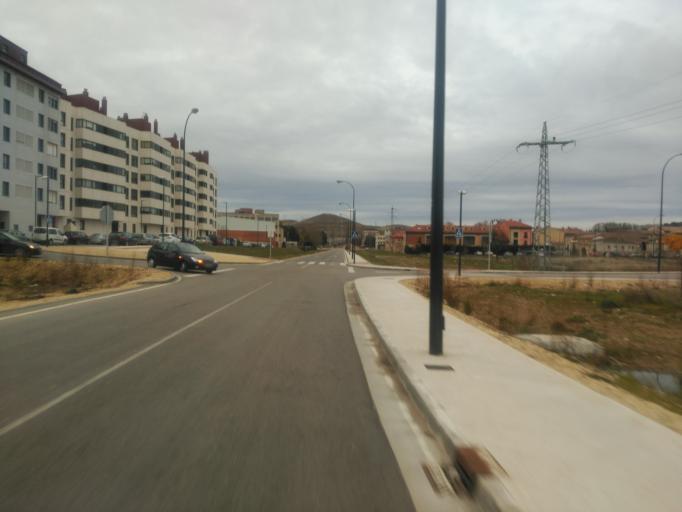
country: ES
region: Castille and Leon
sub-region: Provincia de Burgos
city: Villagonzalo-Pedernales
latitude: 42.3391
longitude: -3.7313
